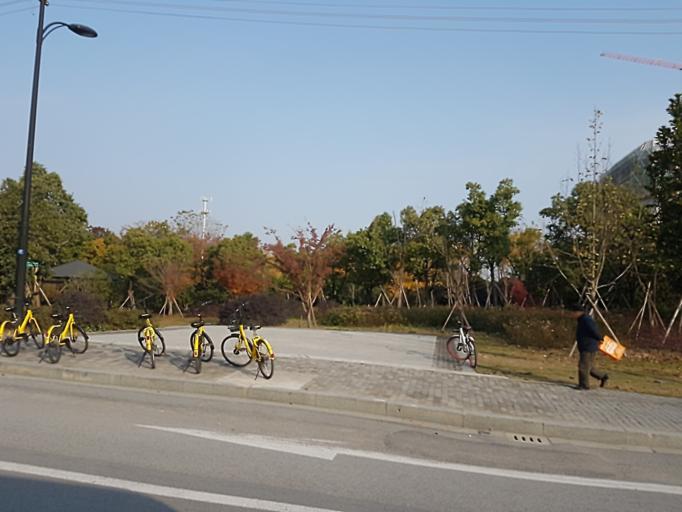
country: CN
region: Zhejiang Sheng
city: Jiangcun
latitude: 30.2969
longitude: 120.0698
